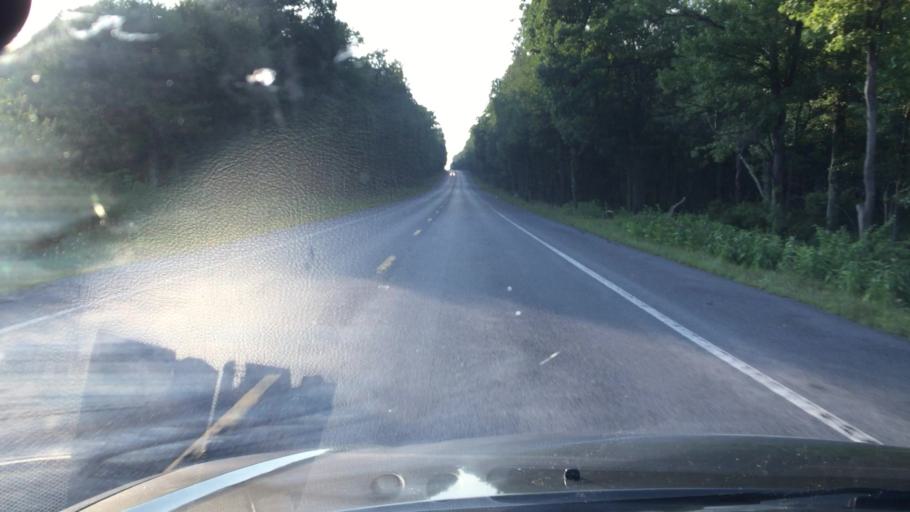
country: US
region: Pennsylvania
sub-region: Carbon County
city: Nesquehoning
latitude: 40.8944
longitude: -75.8091
